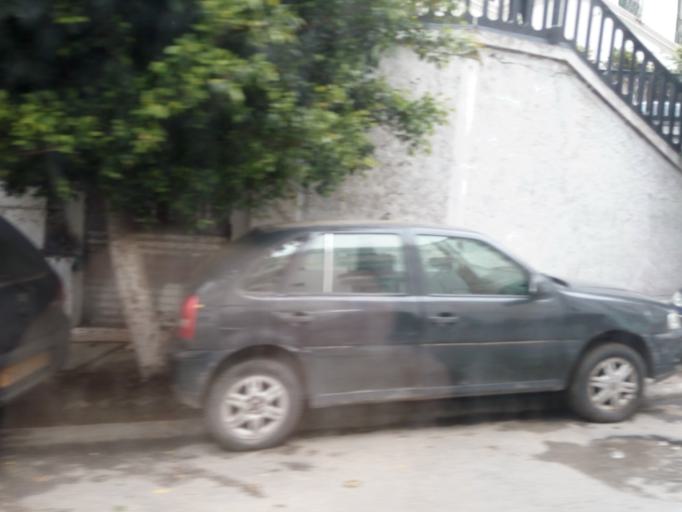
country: DZ
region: Alger
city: Algiers
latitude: 36.7808
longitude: 3.0567
